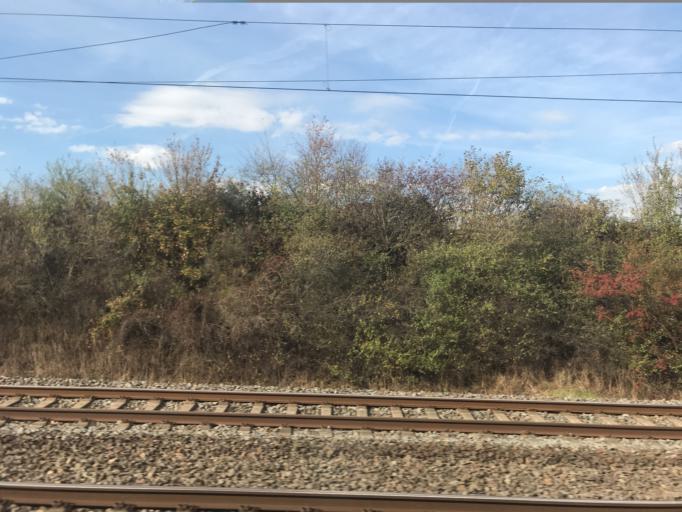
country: DE
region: North Rhine-Westphalia
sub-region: Regierungsbezirk Koln
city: Merzenich
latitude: 50.8448
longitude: 6.5285
